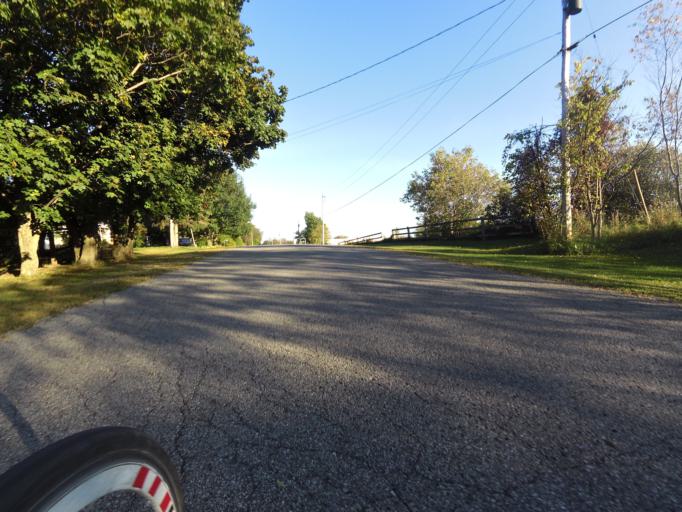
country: CA
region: Ontario
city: Bells Corners
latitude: 45.2271
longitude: -75.7282
